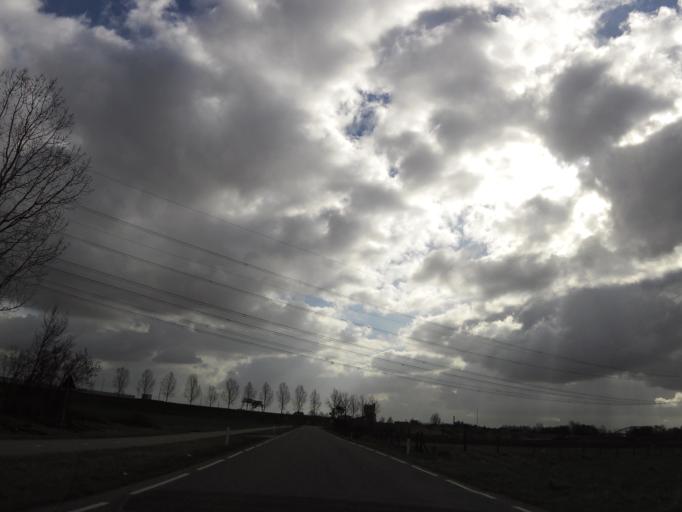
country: NL
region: Limburg
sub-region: Gemeente Sittard-Geleen
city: Born
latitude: 51.0651
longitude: 5.8087
